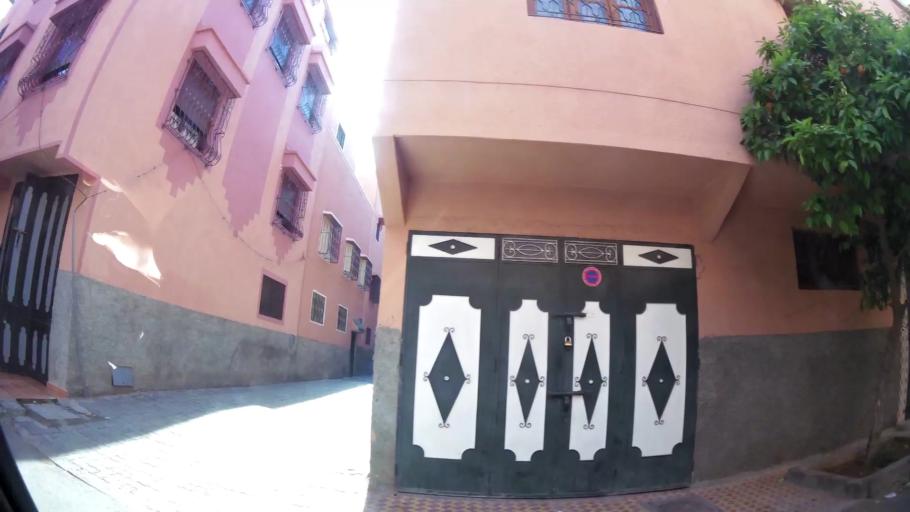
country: MA
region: Marrakech-Tensift-Al Haouz
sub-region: Marrakech
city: Marrakesh
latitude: 31.6451
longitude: -8.0037
